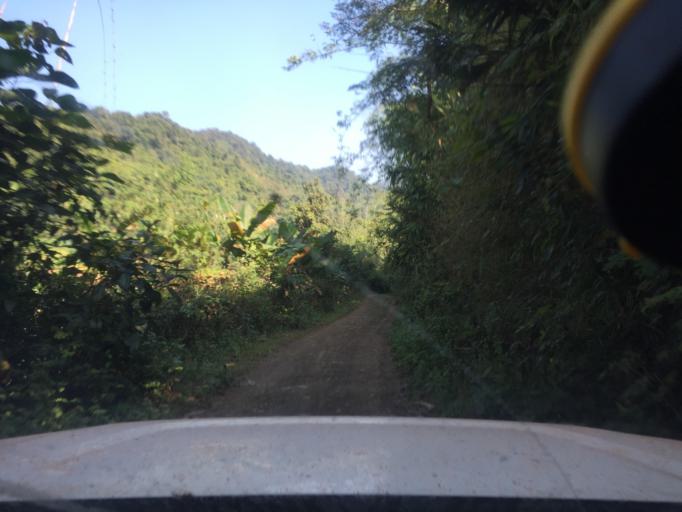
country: LA
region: Phongsali
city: Phongsali
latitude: 21.7036
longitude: 102.3980
